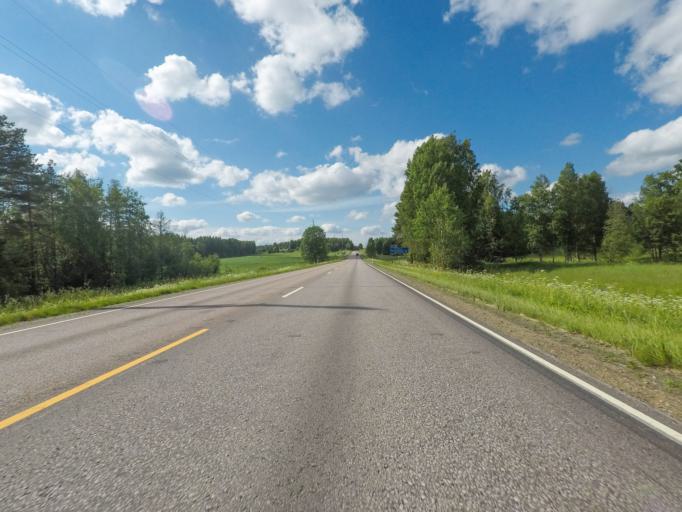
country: FI
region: Southern Savonia
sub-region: Savonlinna
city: Kerimaeki
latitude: 61.8652
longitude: 29.1385
